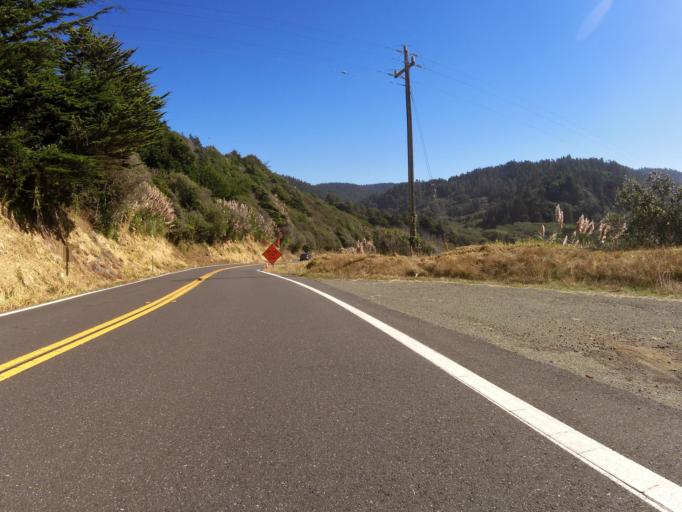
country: US
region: California
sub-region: Mendocino County
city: Fort Bragg
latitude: 39.6523
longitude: -123.7836
